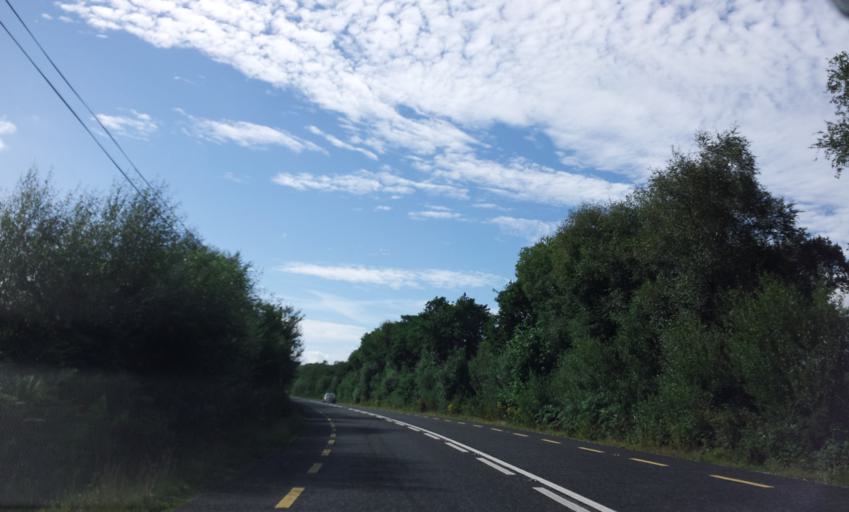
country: IE
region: Munster
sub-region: County Cork
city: Macroom
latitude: 51.9087
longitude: -9.0115
